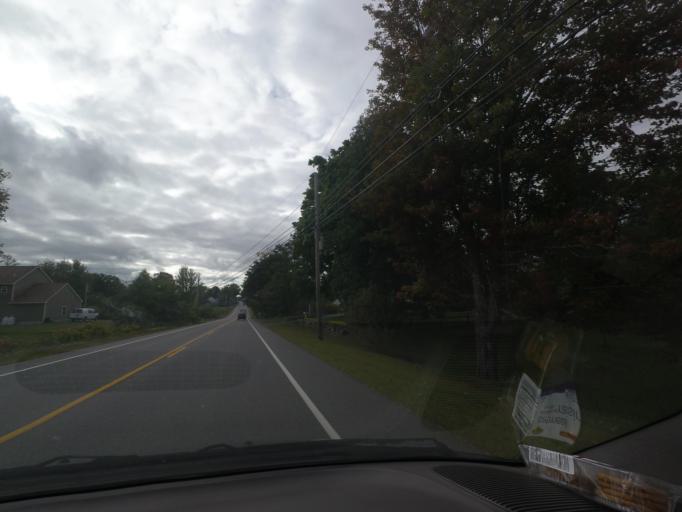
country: US
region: Maine
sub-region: Cumberland County
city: Gorham
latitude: 43.6792
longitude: -70.4522
